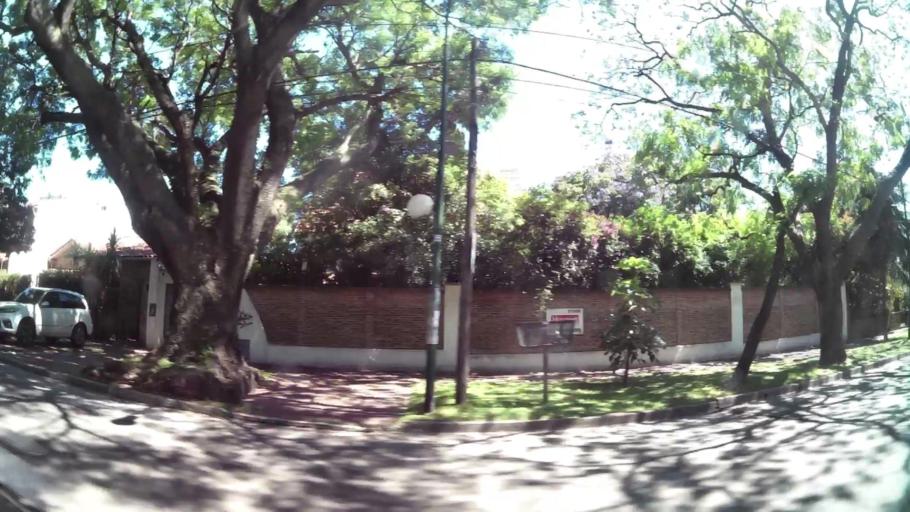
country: AR
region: Buenos Aires
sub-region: Partido de Vicente Lopez
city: Olivos
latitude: -34.4966
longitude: -58.4951
